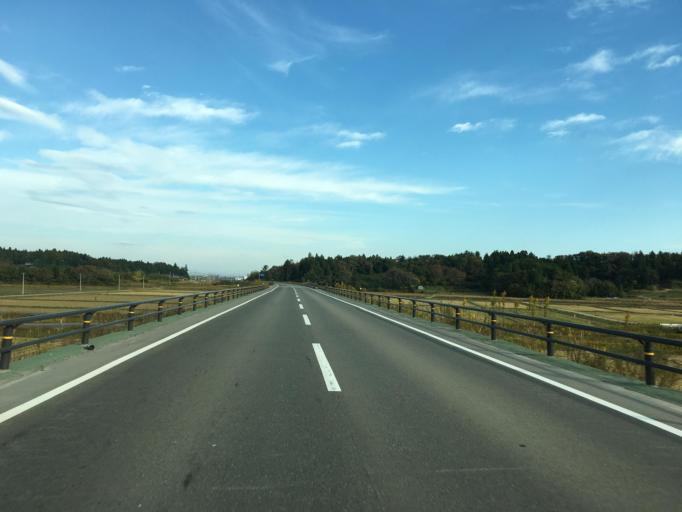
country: JP
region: Miyagi
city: Marumori
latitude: 37.8907
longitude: 140.9255
